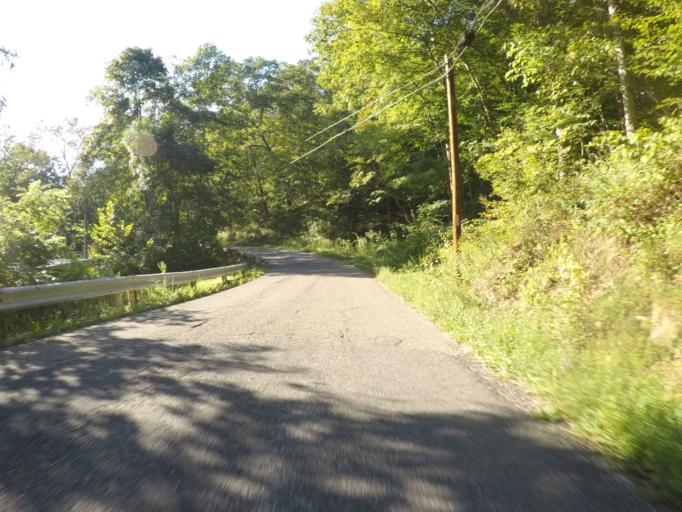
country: US
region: West Virginia
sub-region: Cabell County
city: Huntington
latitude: 38.4759
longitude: -82.4619
